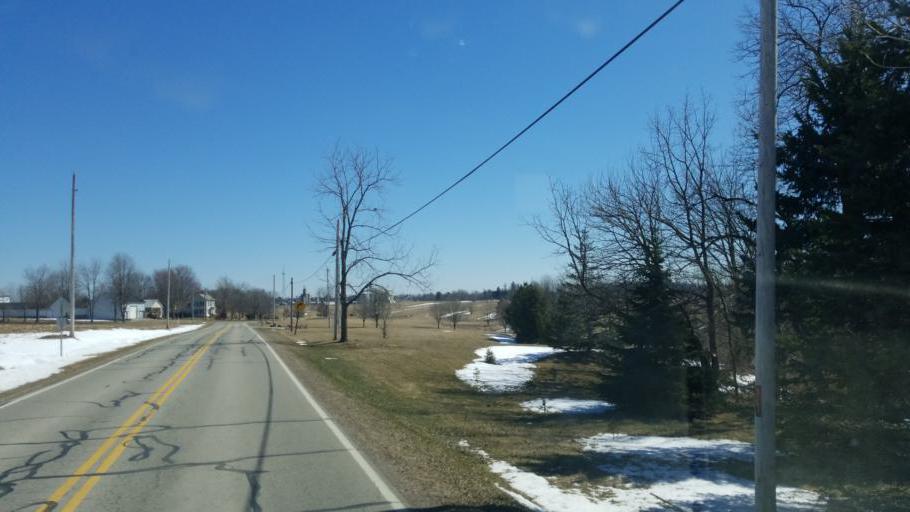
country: US
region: Ohio
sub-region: Crawford County
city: Bucyrus
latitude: 40.8061
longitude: -83.0069
